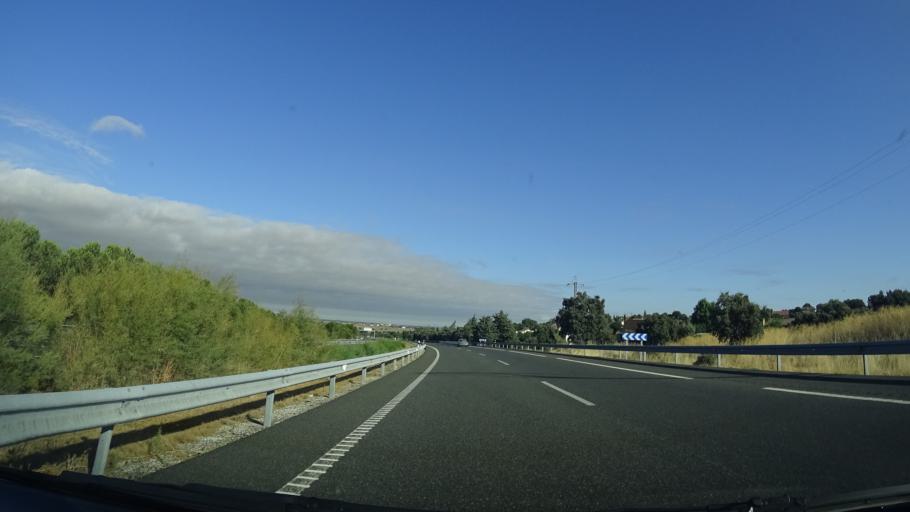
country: ES
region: Castille and Leon
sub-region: Provincia de Segovia
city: Labajos
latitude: 40.8549
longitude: -4.5472
